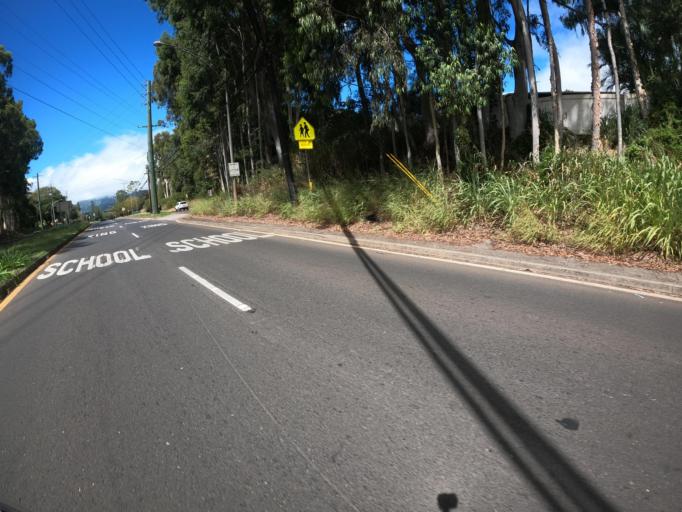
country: US
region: Hawaii
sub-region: Honolulu County
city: Wahiawa
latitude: 21.4875
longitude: -158.0399
